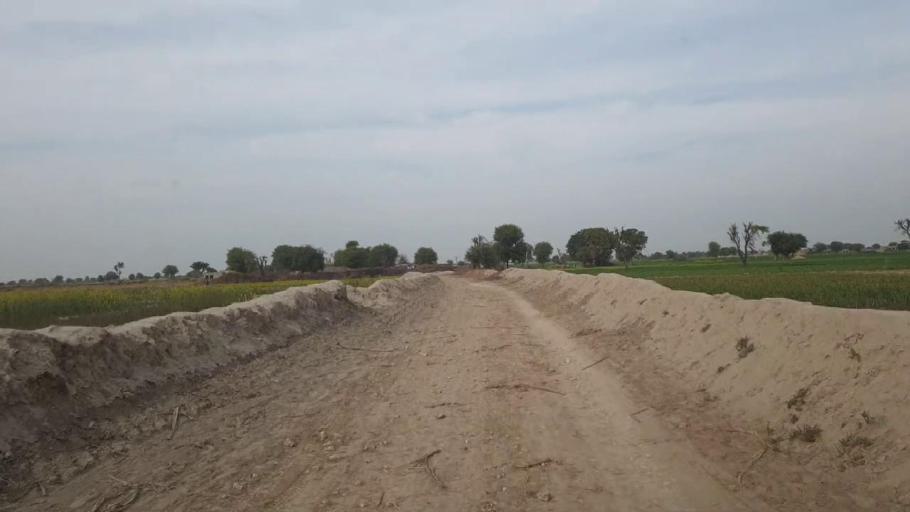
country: PK
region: Sindh
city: Shahpur Chakar
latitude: 26.1204
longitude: 68.5102
